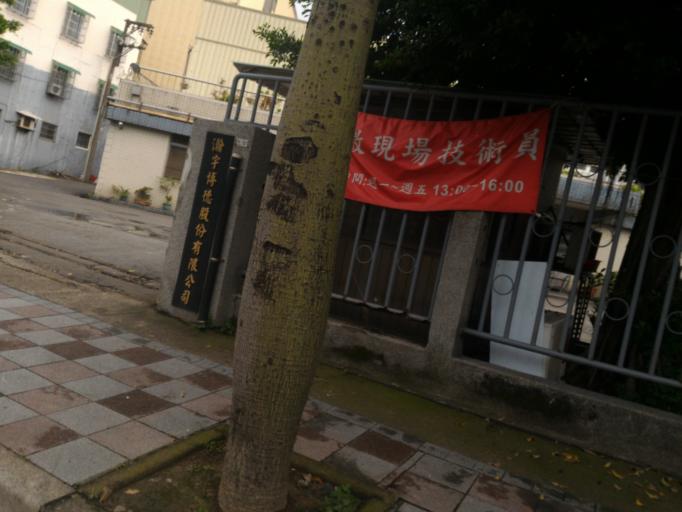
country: TW
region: Taiwan
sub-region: Taoyuan
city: Taoyuan
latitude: 24.9572
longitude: 121.3900
